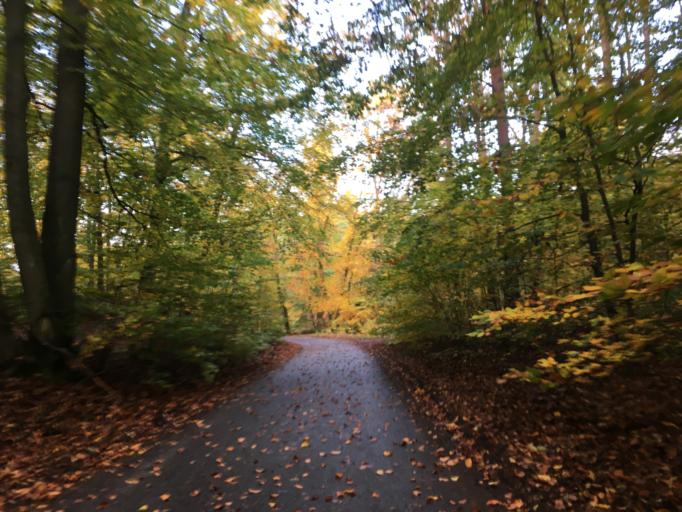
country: DE
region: Brandenburg
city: Wandlitz
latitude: 52.7292
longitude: 13.4613
